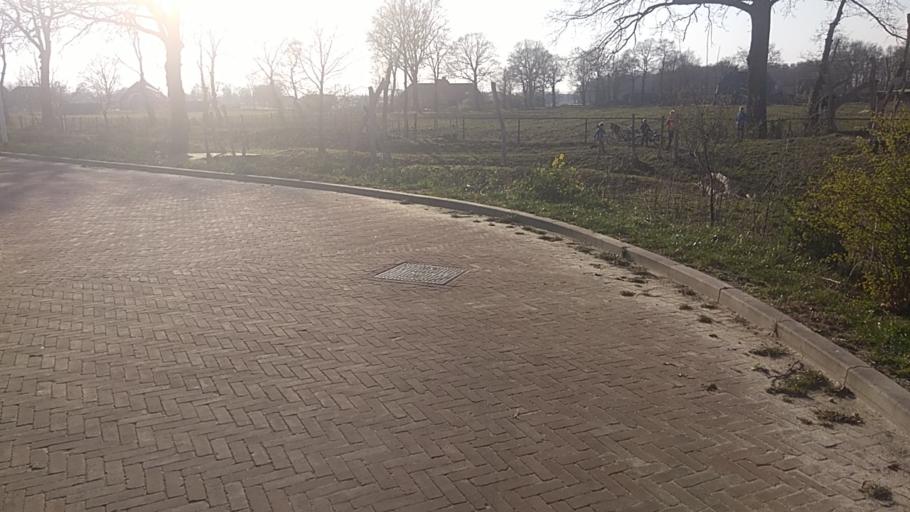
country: NL
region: Overijssel
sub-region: Gemeente Almelo
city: Almelo
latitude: 52.3855
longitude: 6.7104
